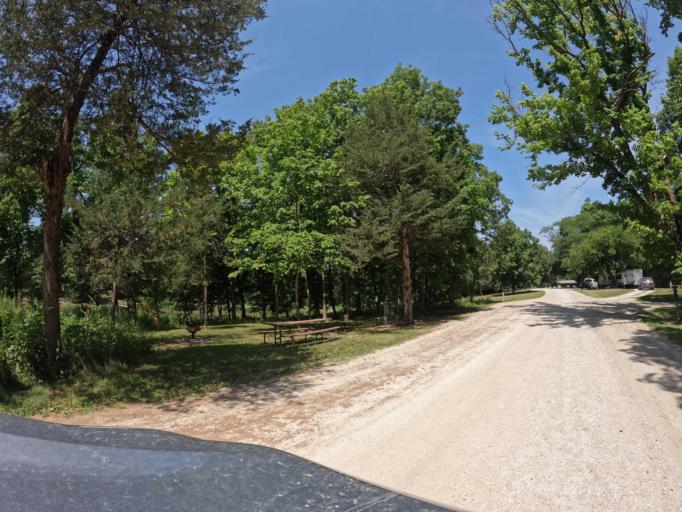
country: US
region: Iowa
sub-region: Henry County
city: Mount Pleasant
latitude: 40.9313
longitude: -91.6157
